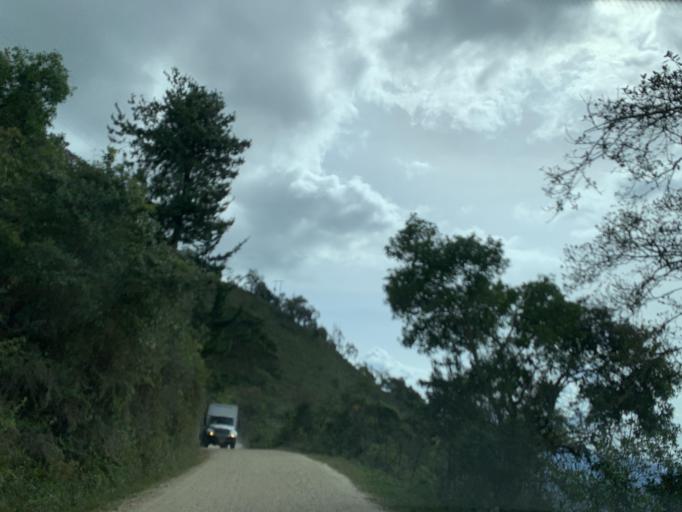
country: CO
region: Santander
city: Capitanejo
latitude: 6.5039
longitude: -72.7342
